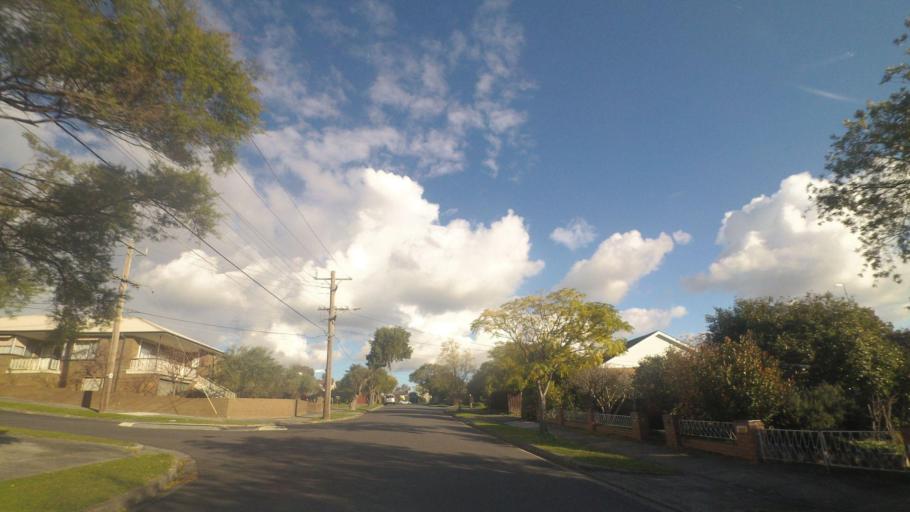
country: AU
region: Victoria
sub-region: Boroondara
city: Balwyn North
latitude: -37.7817
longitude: 145.1064
